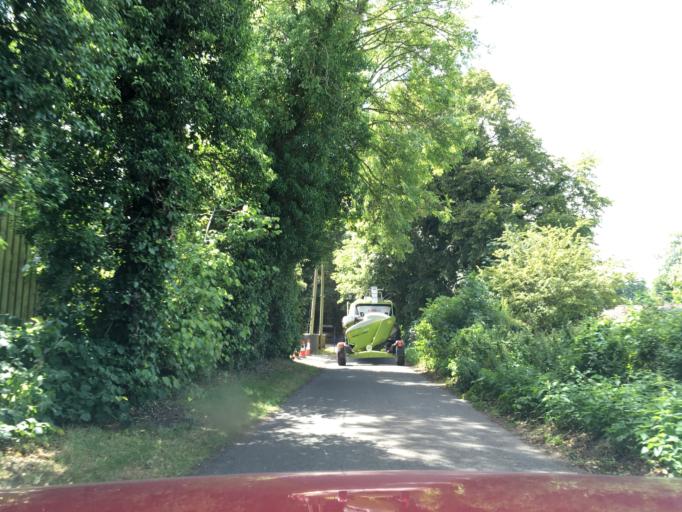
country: GB
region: England
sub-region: Wiltshire
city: Biddestone
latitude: 51.5142
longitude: -2.1982
